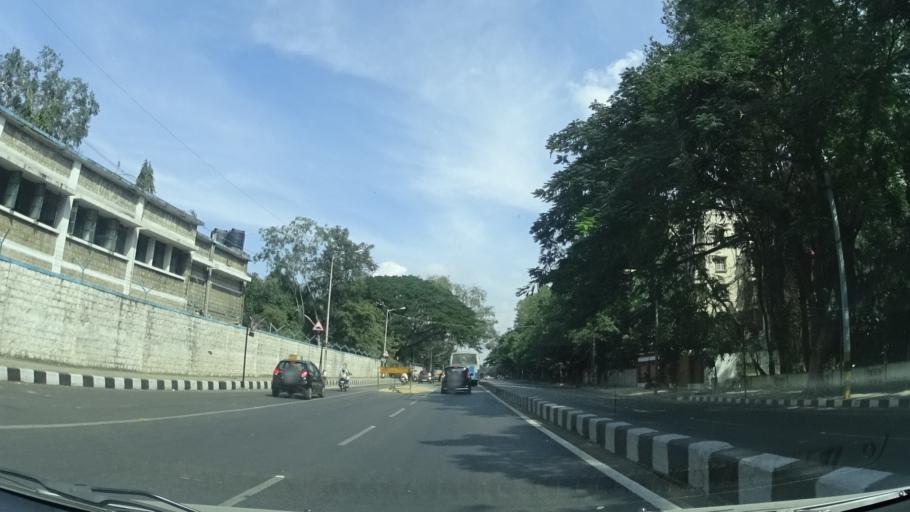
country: IN
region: Karnataka
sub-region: Bangalore Urban
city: Bangalore
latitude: 13.0150
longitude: 77.5786
